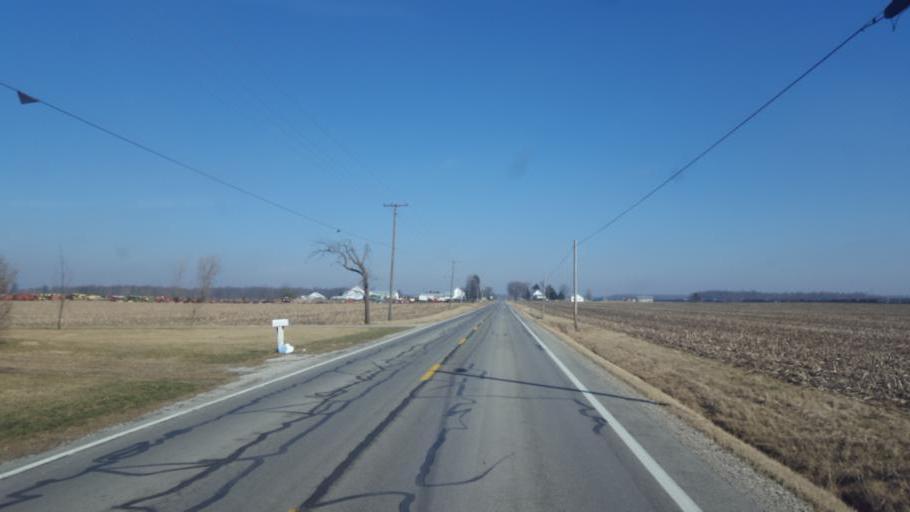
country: US
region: Ohio
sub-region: Huron County
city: Willard
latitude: 41.0313
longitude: -82.9042
